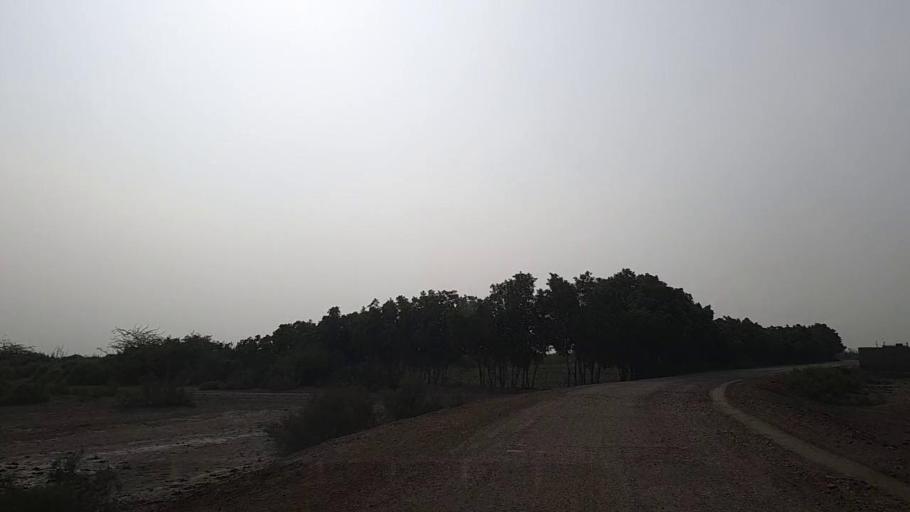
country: PK
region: Sindh
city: Mirpur Sakro
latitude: 24.6446
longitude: 67.6146
